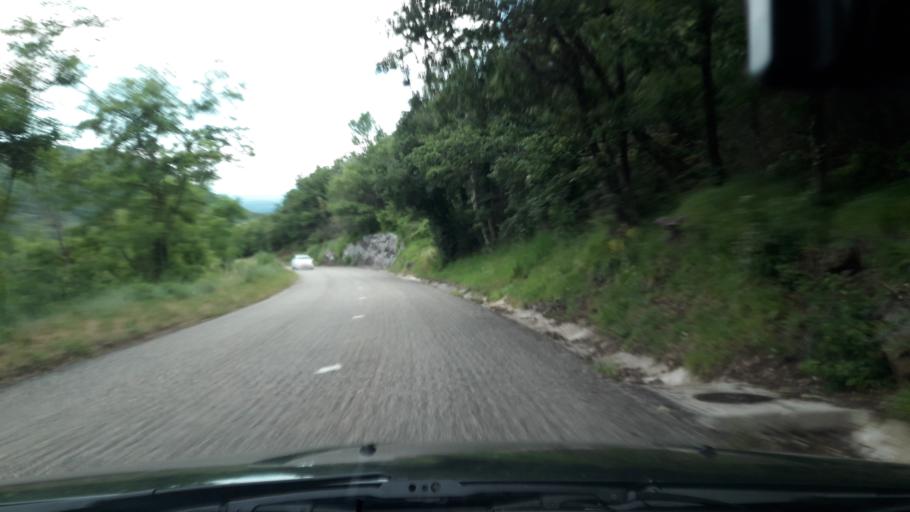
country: FR
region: Rhone-Alpes
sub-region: Departement de l'Ardeche
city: Saint-Priest
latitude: 44.6564
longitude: 4.5251
